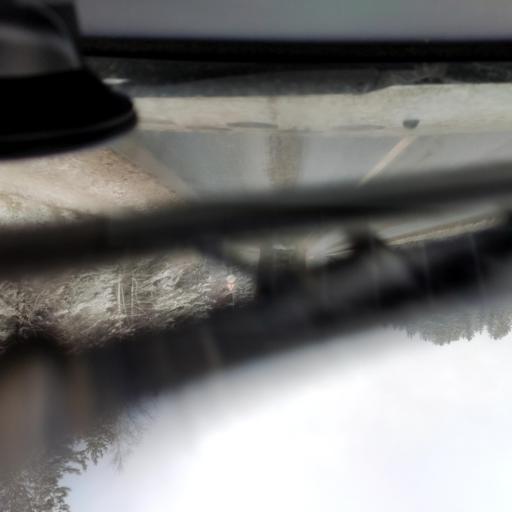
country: RU
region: Perm
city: Nytva
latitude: 57.9687
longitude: 55.3643
